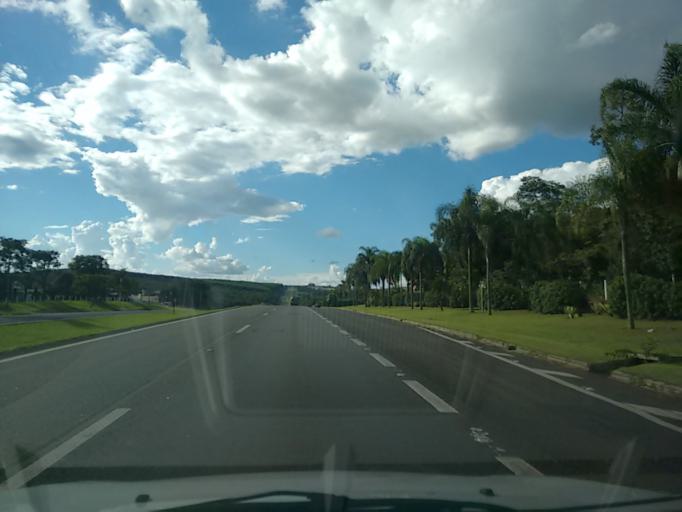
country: BR
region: Sao Paulo
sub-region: Sao Carlos
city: Sao Carlos
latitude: -22.0721
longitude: -47.8444
